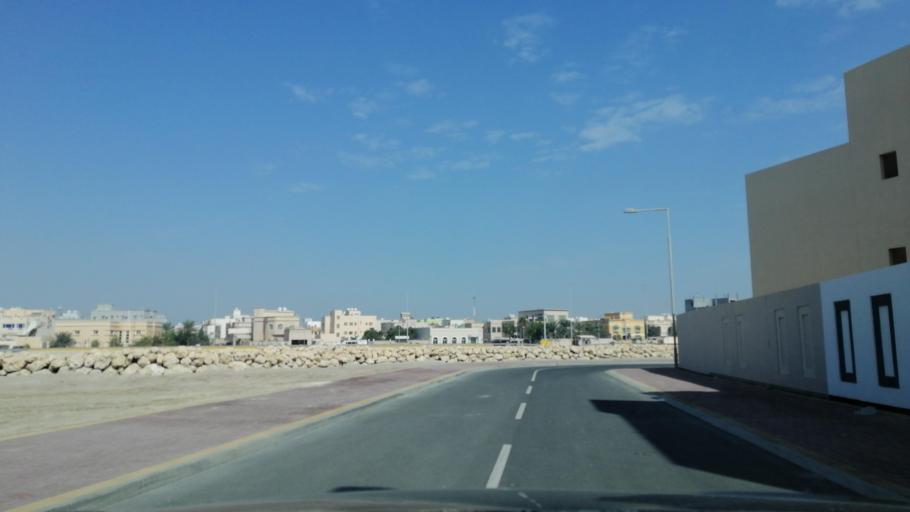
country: BH
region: Muharraq
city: Al Hadd
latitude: 26.2422
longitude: 50.6338
